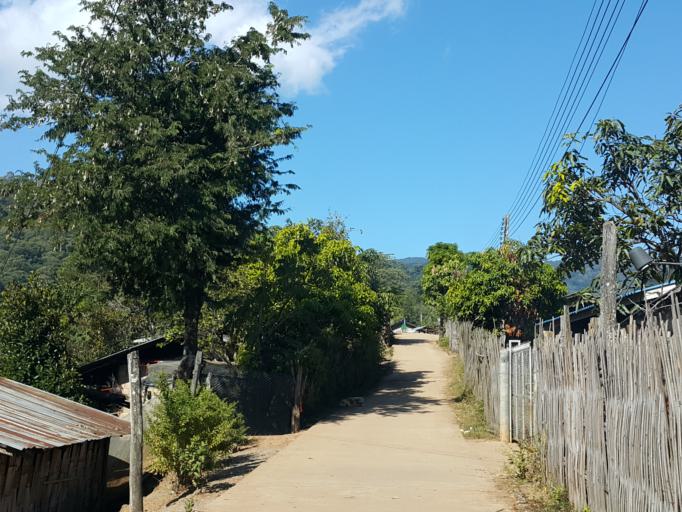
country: TH
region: Chiang Mai
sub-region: Amphoe Chiang Dao
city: Chiang Dao
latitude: 19.5251
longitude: 98.8618
